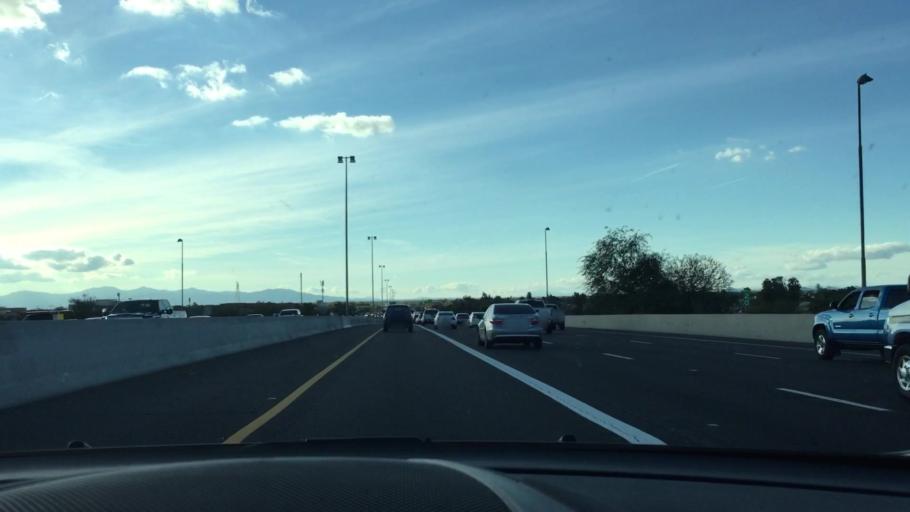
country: US
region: Arizona
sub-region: Maricopa County
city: Peoria
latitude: 33.6665
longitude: -112.1723
